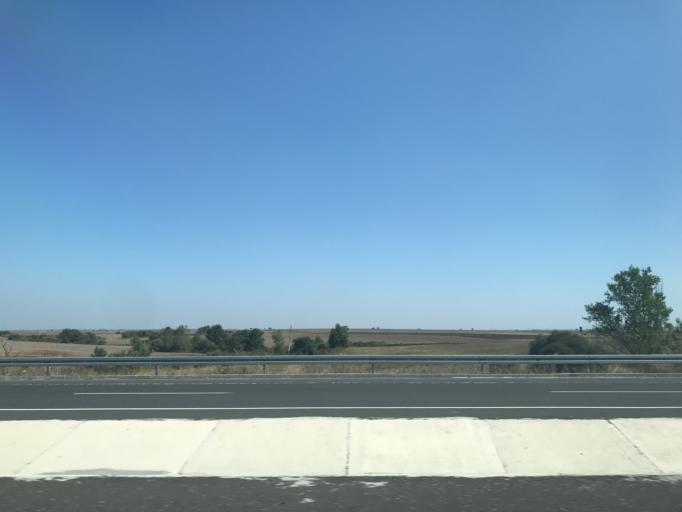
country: TR
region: Tekirdag
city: Muratli
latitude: 41.1802
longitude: 27.5389
